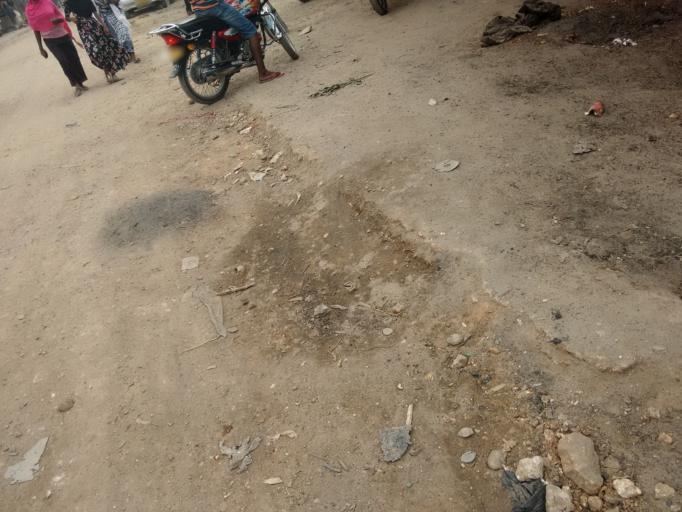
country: TZ
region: Dar es Salaam
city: Dar es Salaam
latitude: -6.8603
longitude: 39.2513
